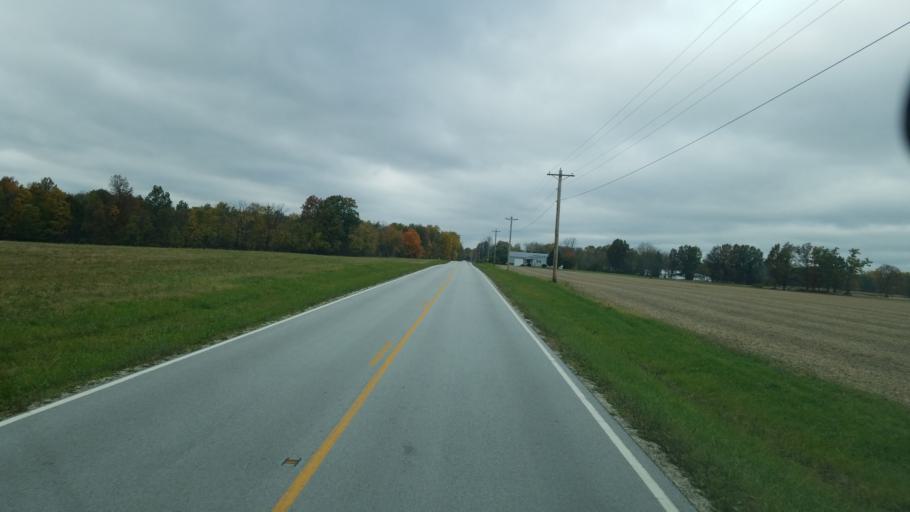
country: US
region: Ohio
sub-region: Sandusky County
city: Mount Carmel
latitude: 41.0665
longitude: -82.9406
